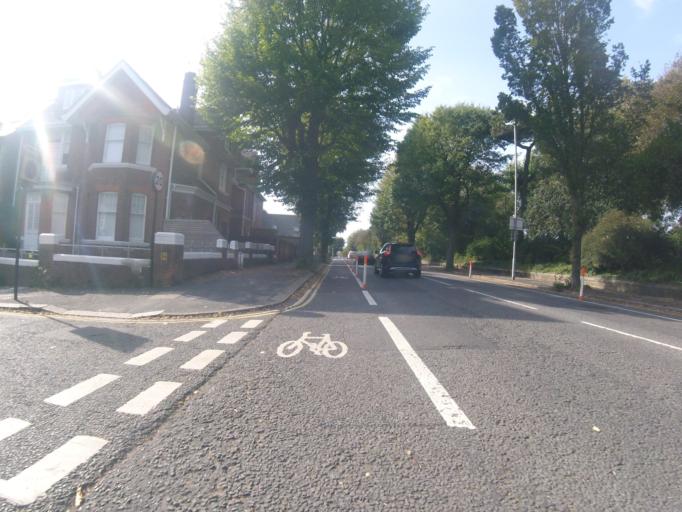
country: GB
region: England
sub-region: Brighton and Hove
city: Hove
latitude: 50.8378
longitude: -0.1674
